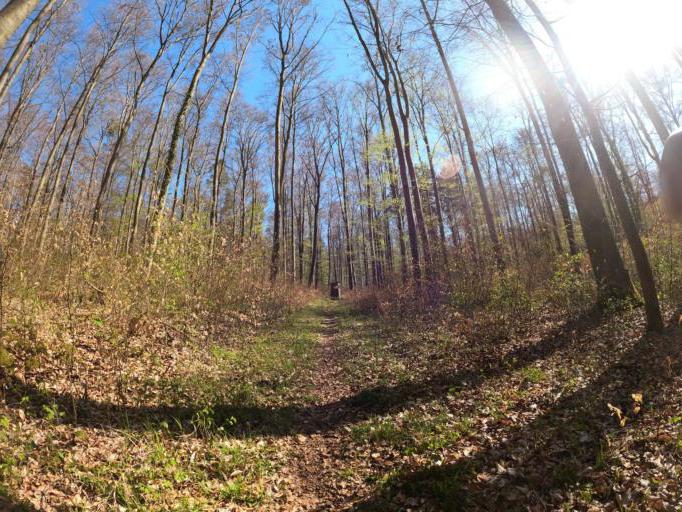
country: DE
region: Baden-Wuerttemberg
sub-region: Karlsruhe Region
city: Monsheim
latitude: 48.9042
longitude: 8.9047
